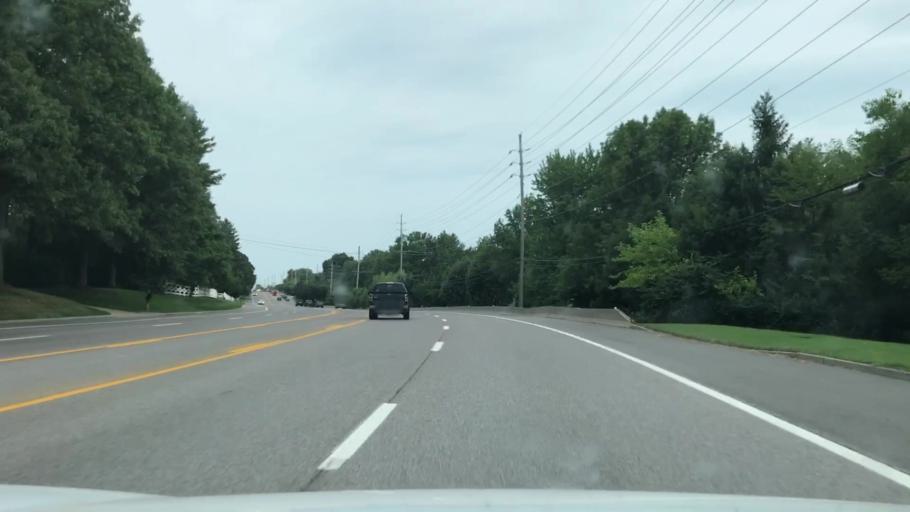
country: US
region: Missouri
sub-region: Saint Louis County
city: Clarkson Valley
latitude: 38.6156
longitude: -90.5855
